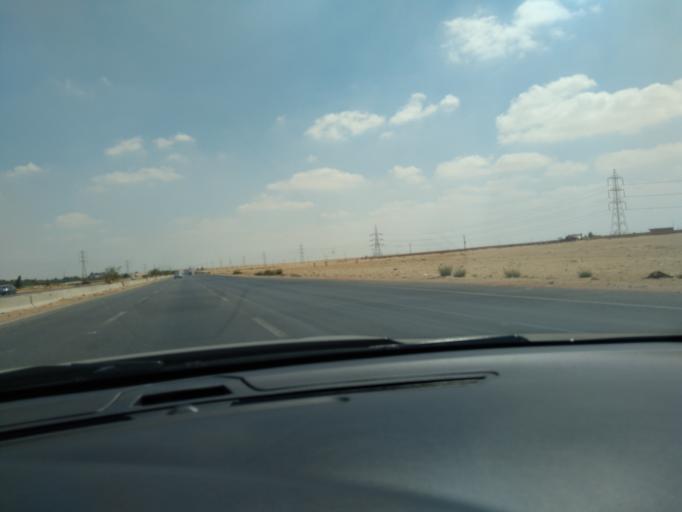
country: EG
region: Al Isma'iliyah
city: At Tall al Kabir
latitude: 30.3598
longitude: 31.9035
